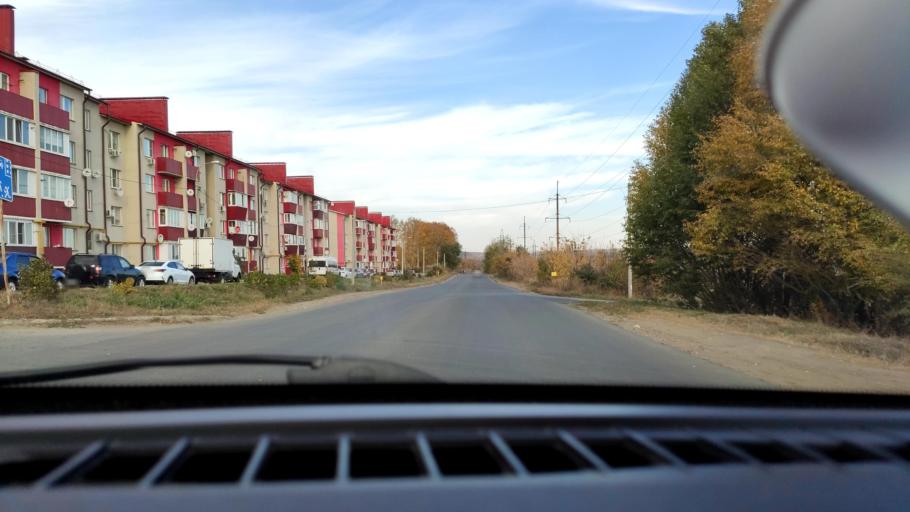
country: RU
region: Samara
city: Novosemeykino
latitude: 53.3311
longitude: 50.3151
